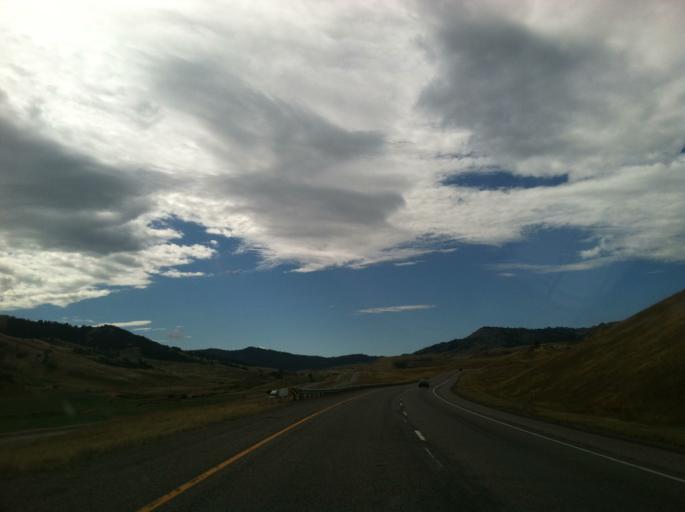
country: US
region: Montana
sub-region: Park County
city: Livingston
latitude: 45.6628
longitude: -110.7052
